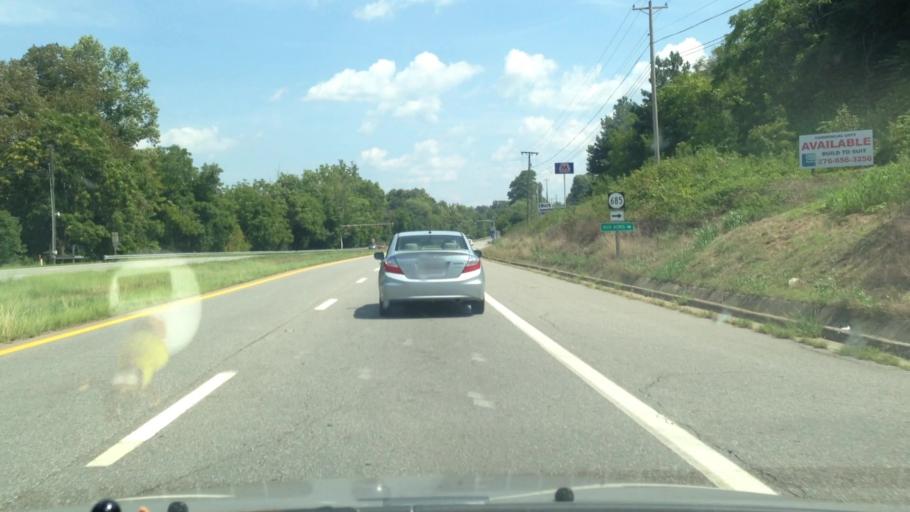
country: US
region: Virginia
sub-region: City of Martinsville
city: Martinsville
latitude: 36.6516
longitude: -79.8720
